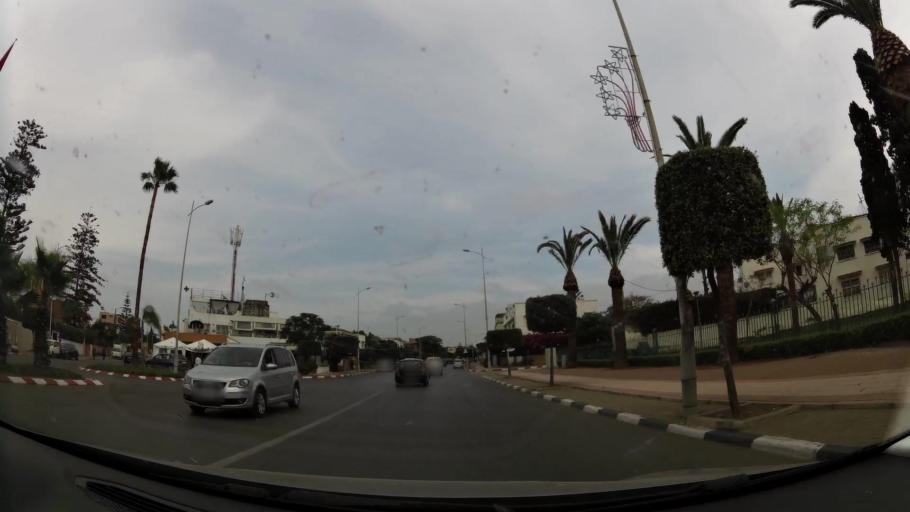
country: MA
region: Rabat-Sale-Zemmour-Zaer
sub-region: Rabat
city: Rabat
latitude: 34.0307
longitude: -6.8133
